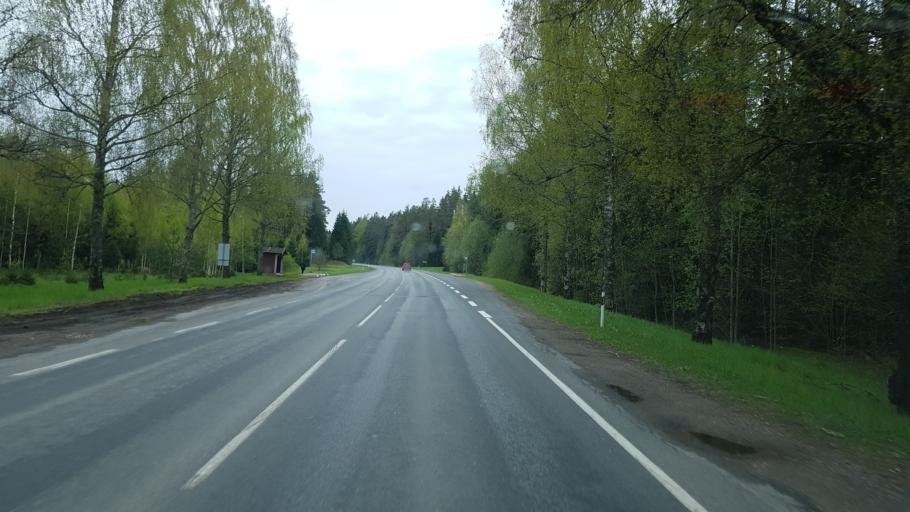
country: EE
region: Viljandimaa
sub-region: Viljandi linn
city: Viljandi
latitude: 58.3009
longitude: 25.5744
